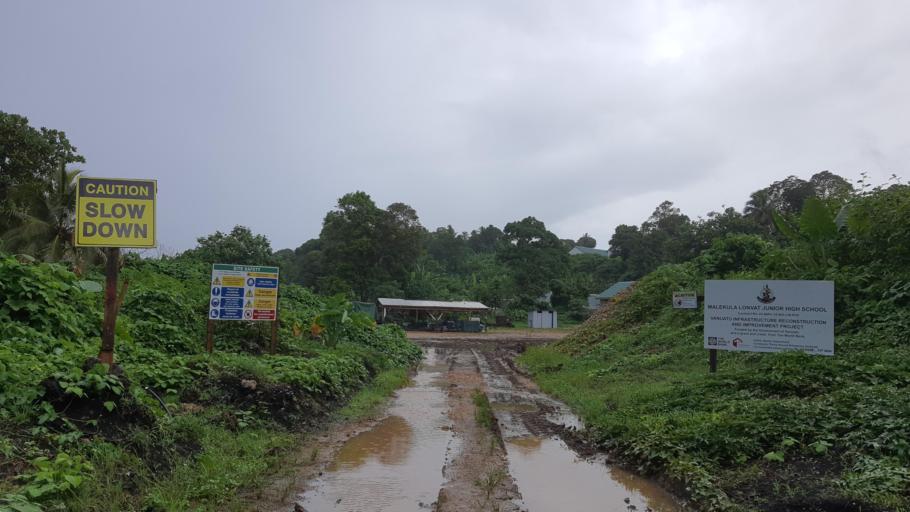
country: VU
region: Malampa
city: Lakatoro
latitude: -16.5012
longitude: 167.6513
